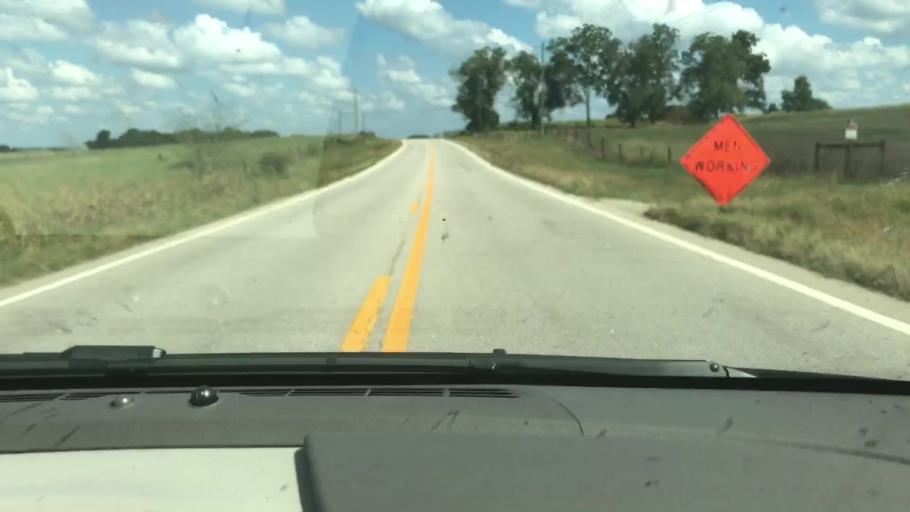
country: US
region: Georgia
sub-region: Troup County
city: West Point
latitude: 32.8812
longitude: -85.0336
